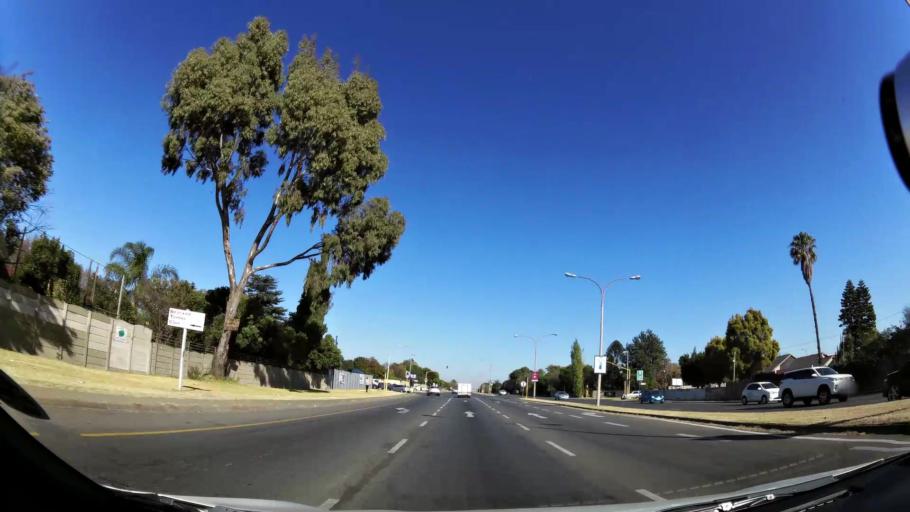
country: ZA
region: Gauteng
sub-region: Ekurhuleni Metropolitan Municipality
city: Germiston
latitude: -26.3077
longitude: 28.1067
